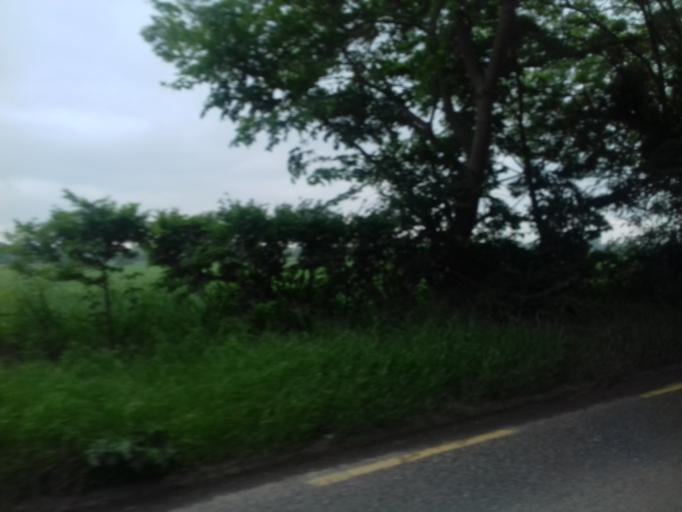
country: IE
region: Leinster
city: Donabate
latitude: 53.4815
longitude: -6.1758
